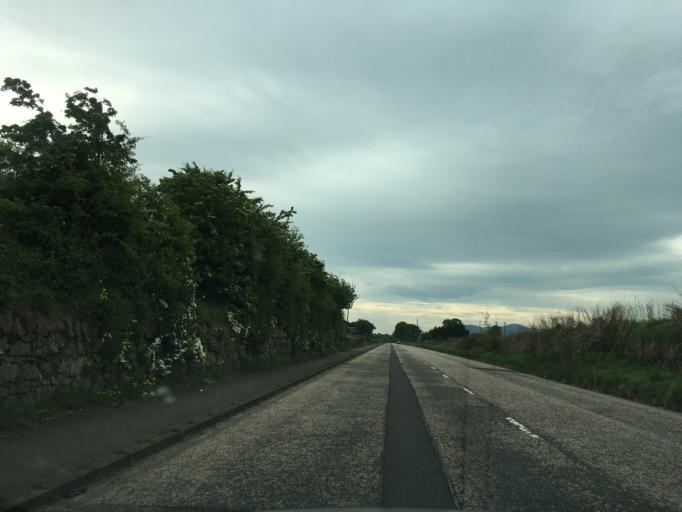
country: GB
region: Scotland
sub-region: Edinburgh
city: Currie
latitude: 55.9478
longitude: -3.3297
